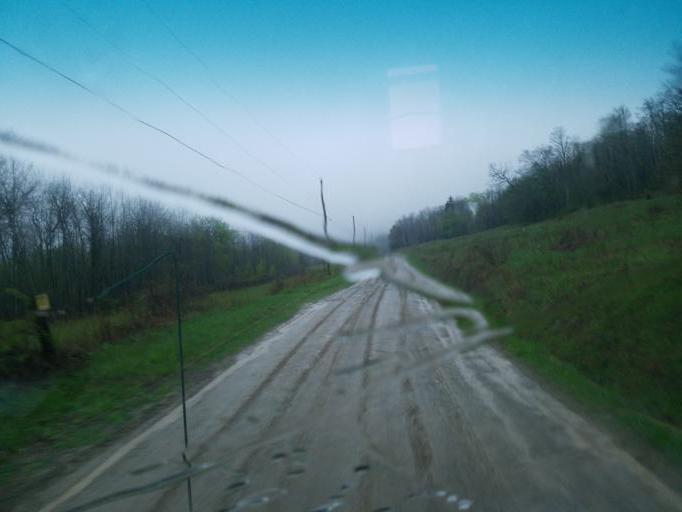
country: US
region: Pennsylvania
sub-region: Tioga County
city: Westfield
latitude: 41.9330
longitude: -77.6943
